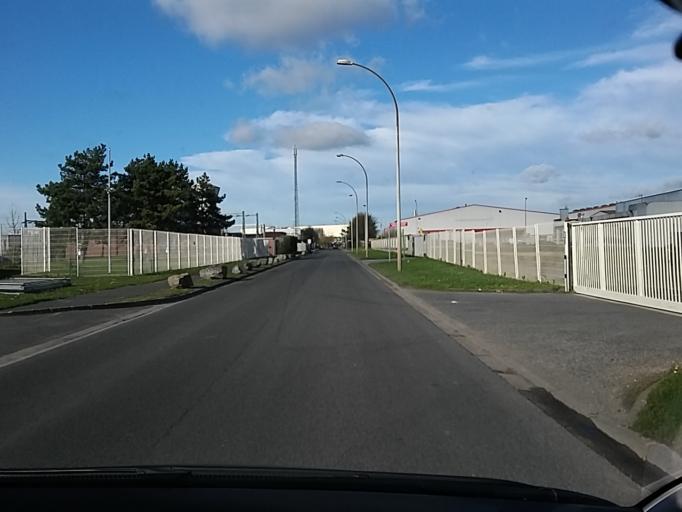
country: FR
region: Picardie
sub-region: Departement de la Somme
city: Dreuil-les-Amiens
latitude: 49.9328
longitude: 2.2667
